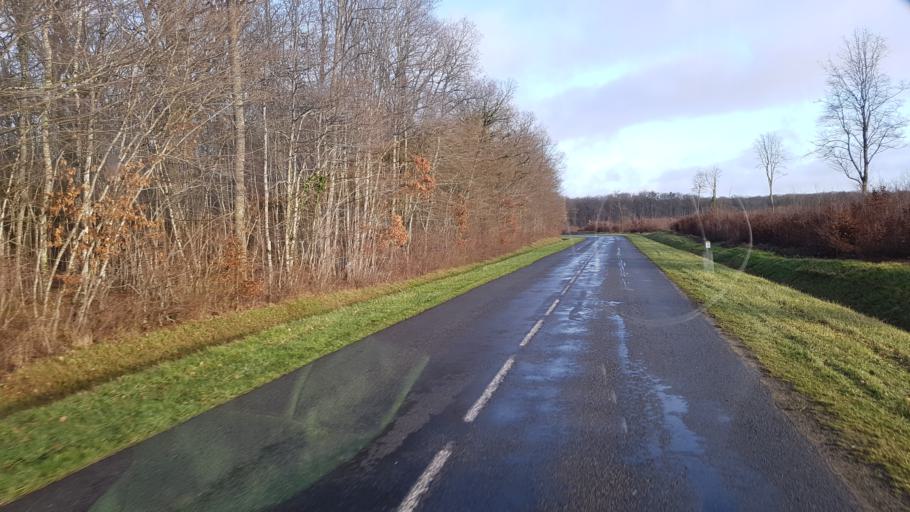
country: FR
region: Centre
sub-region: Departement du Loiret
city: Chilleurs-aux-Bois
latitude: 48.0179
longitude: 2.2048
